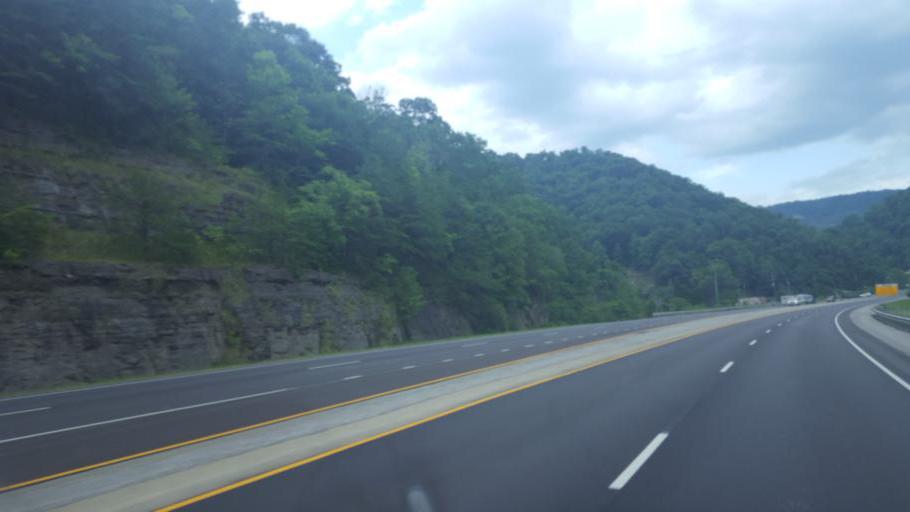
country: US
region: Kentucky
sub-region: Pike County
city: Pikeville
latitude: 37.3178
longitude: -82.5503
